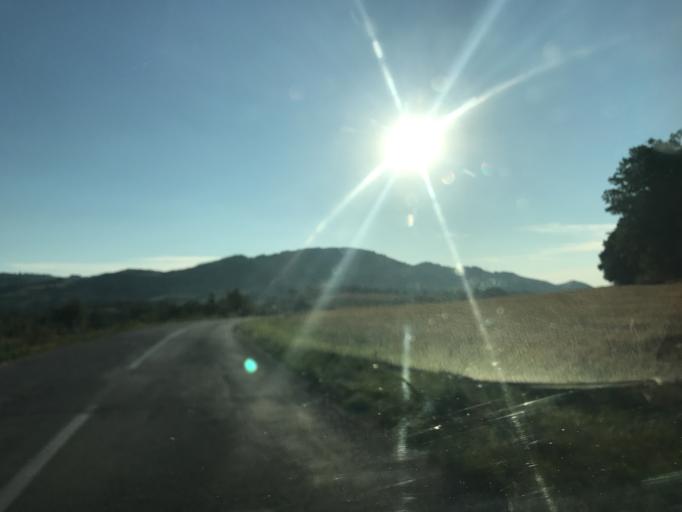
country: RO
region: Mehedinti
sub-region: Comuna Svinita
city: Svinita
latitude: 44.3056
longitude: 22.2328
